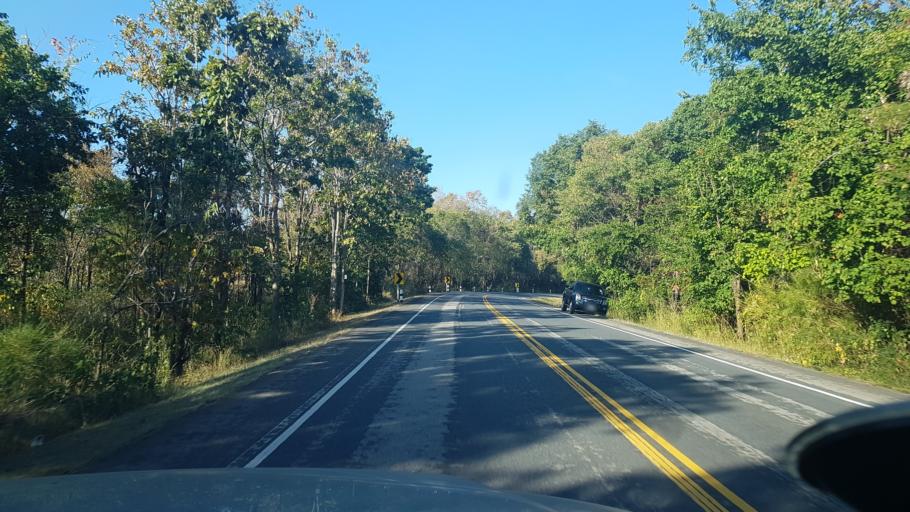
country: TH
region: Phetchabun
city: Lom Sak
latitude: 16.7366
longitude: 101.4217
